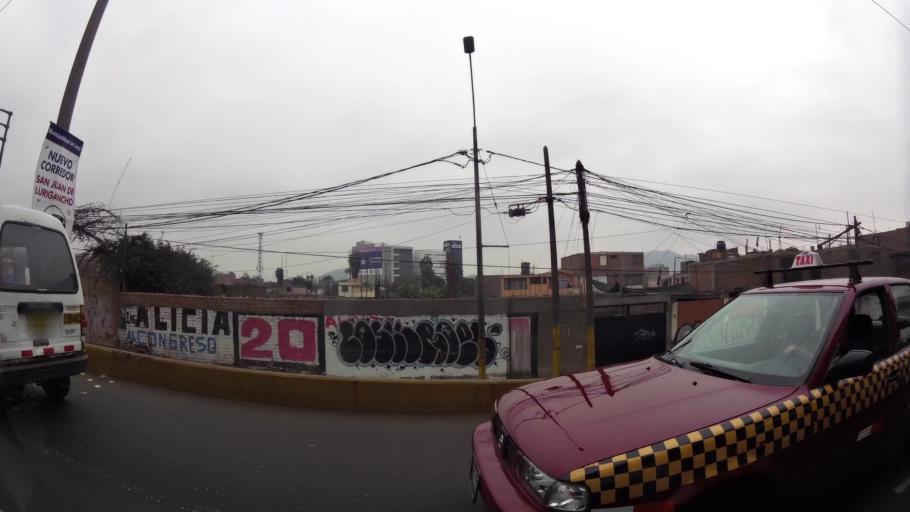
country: PE
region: Lima
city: Lima
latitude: -12.0186
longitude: -77.0030
